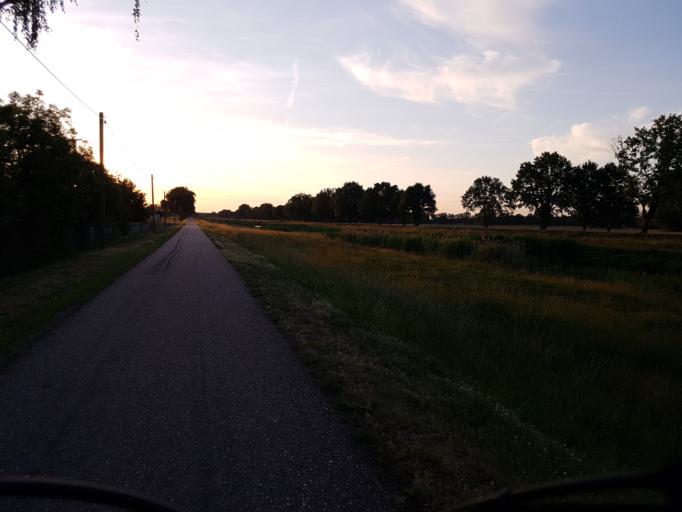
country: DE
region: Brandenburg
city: Falkenberg
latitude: 51.6096
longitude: 13.3053
